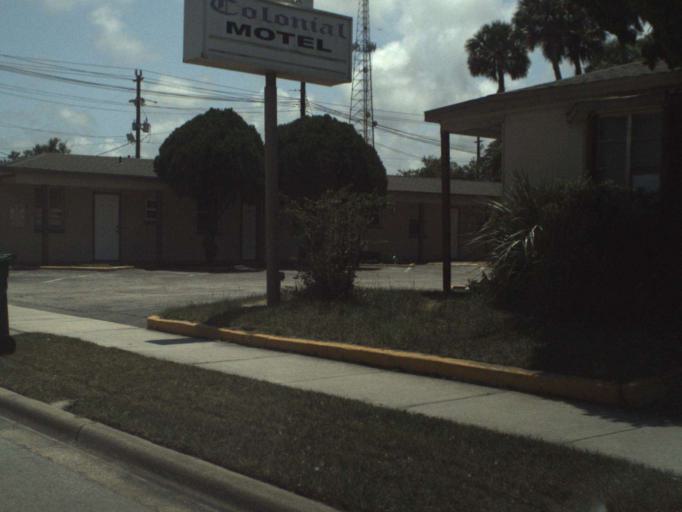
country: US
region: Florida
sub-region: Volusia County
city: Holly Hill
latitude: 29.2296
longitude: -81.0330
